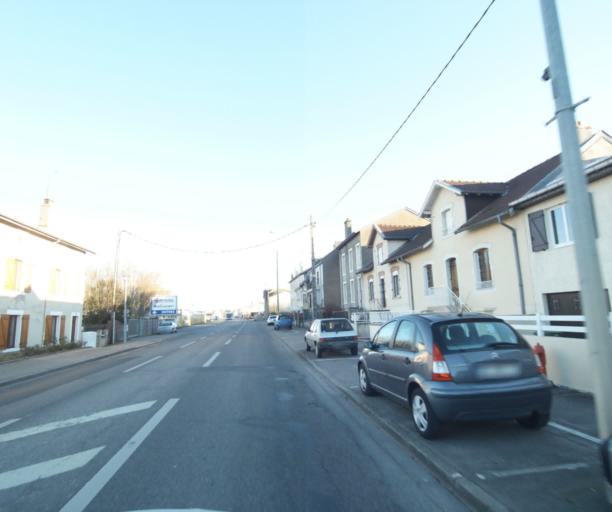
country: FR
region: Lorraine
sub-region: Departement de Meurthe-et-Moselle
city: Heillecourt
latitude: 48.6638
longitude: 6.2186
